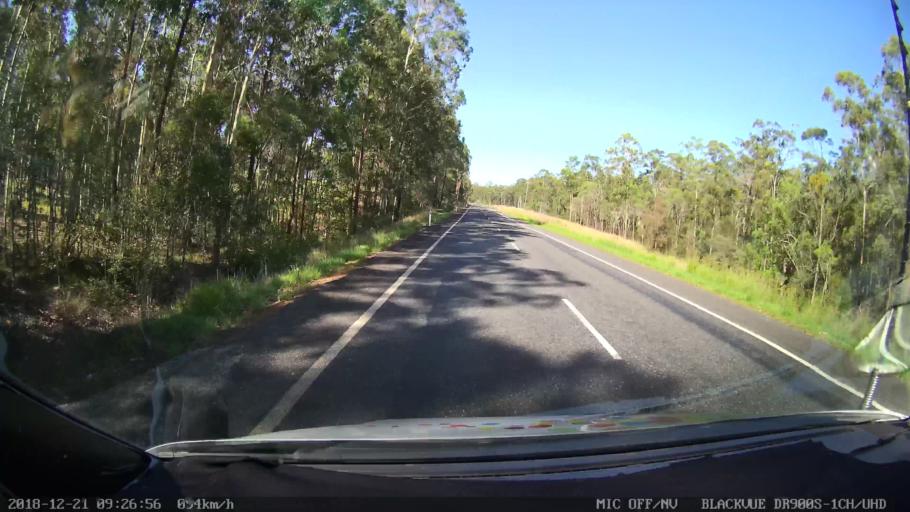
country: AU
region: New South Wales
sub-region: Clarence Valley
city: Maclean
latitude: -29.3976
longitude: 152.9957
